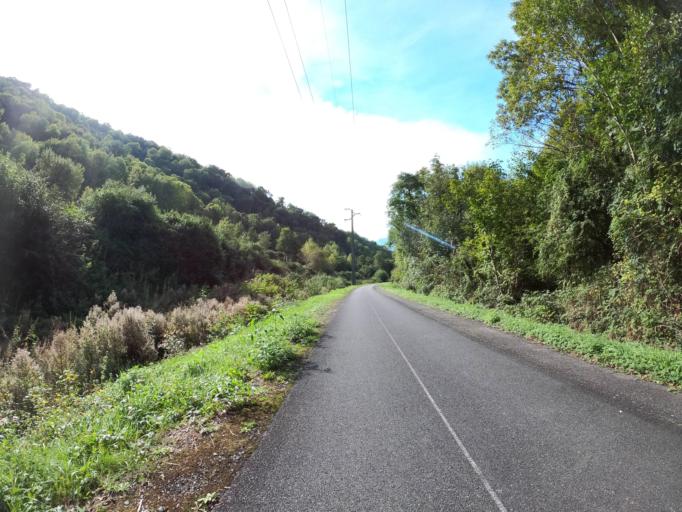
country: FR
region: Midi-Pyrenees
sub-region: Departement des Hautes-Pyrenees
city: Argeles-Gazost
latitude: 43.0288
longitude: -0.0633
